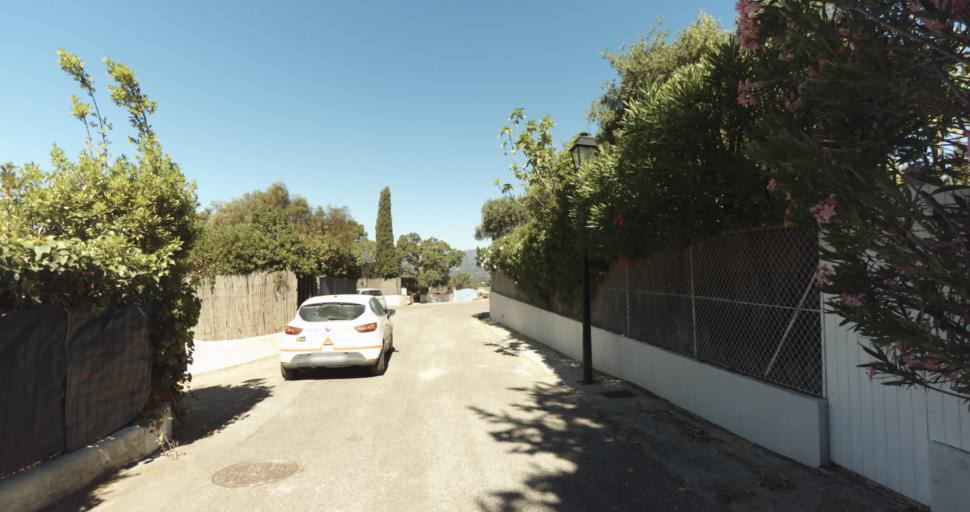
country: FR
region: Provence-Alpes-Cote d'Azur
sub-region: Departement du Var
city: Gassin
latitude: 43.2590
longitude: 6.6039
